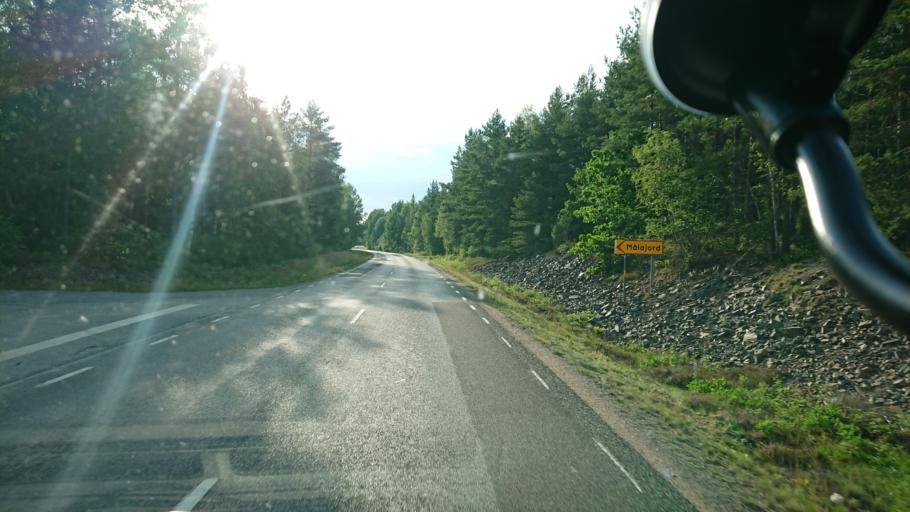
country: SE
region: Kronoberg
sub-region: Vaxjo Kommun
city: Rottne
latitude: 57.0314
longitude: 14.9694
